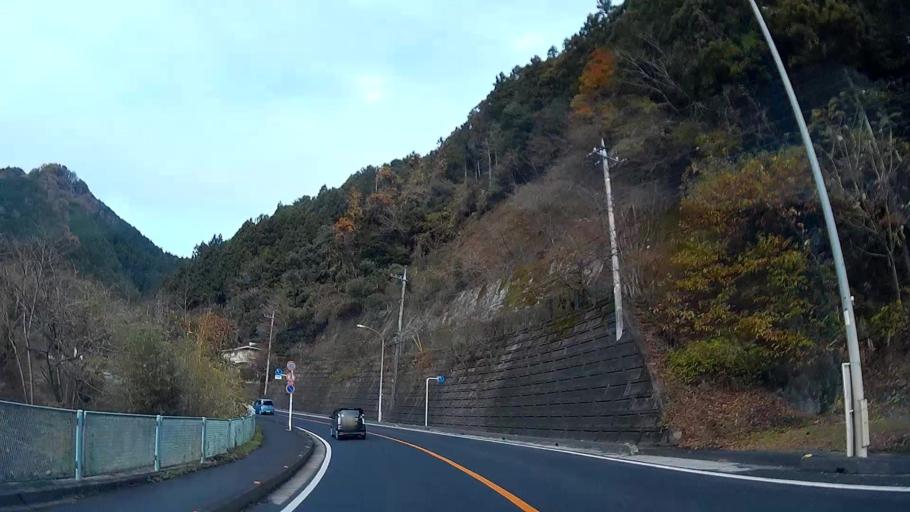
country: JP
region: Saitama
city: Chichibu
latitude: 35.9388
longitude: 139.1828
